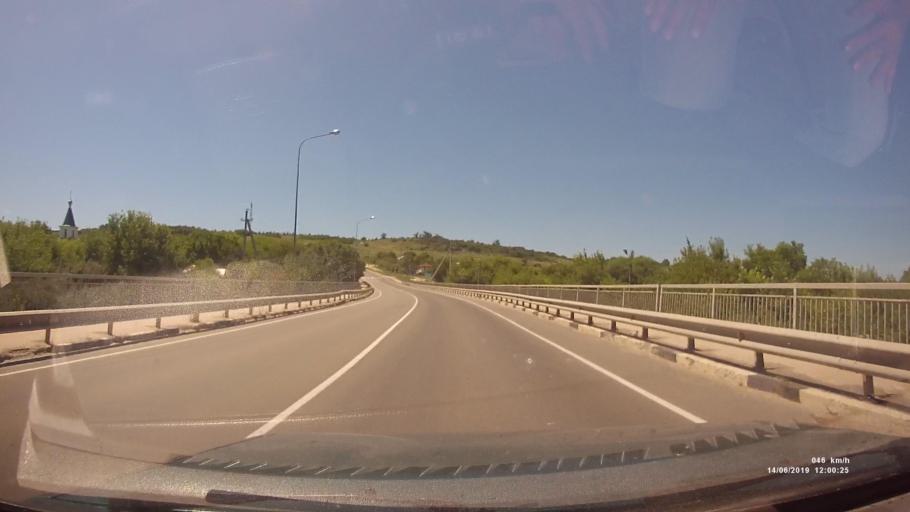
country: RU
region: Rostov
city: Kazanskaya
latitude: 49.7890
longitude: 41.1273
